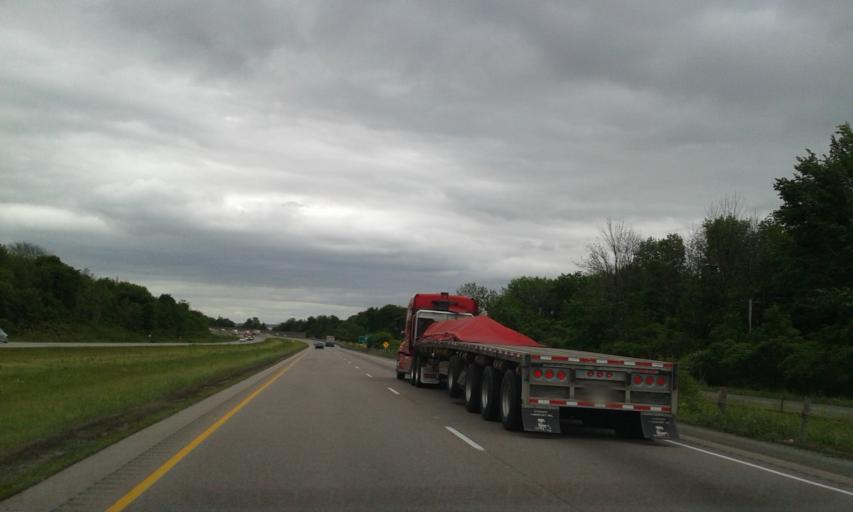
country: CA
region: Ontario
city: Brockville
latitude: 44.5228
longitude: -75.7782
